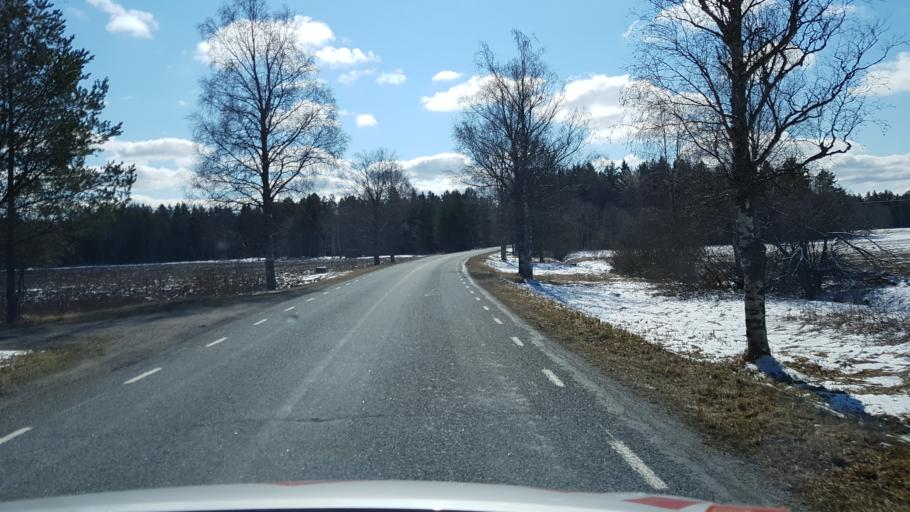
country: EE
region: Laeaene-Virumaa
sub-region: Kadrina vald
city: Kadrina
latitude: 59.4858
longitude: 25.9921
